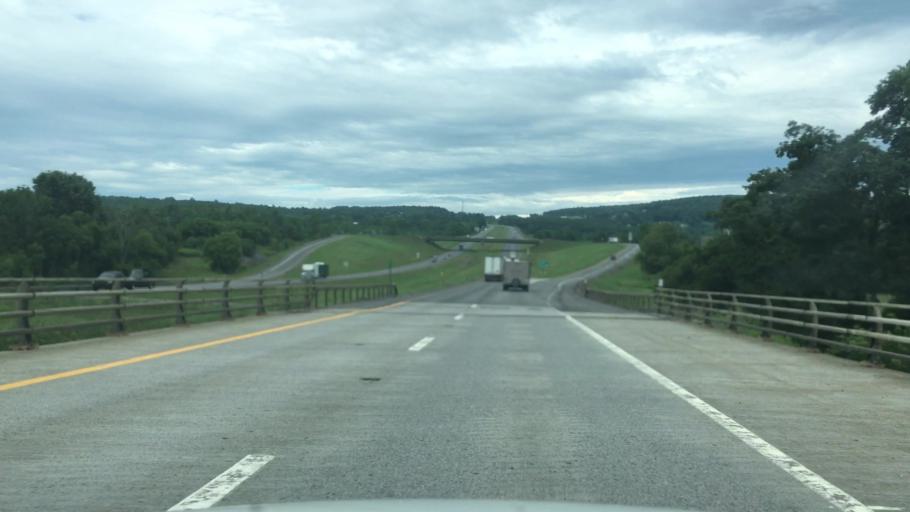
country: US
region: New York
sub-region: Schoharie County
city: Schoharie
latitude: 42.7056
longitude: -74.3216
